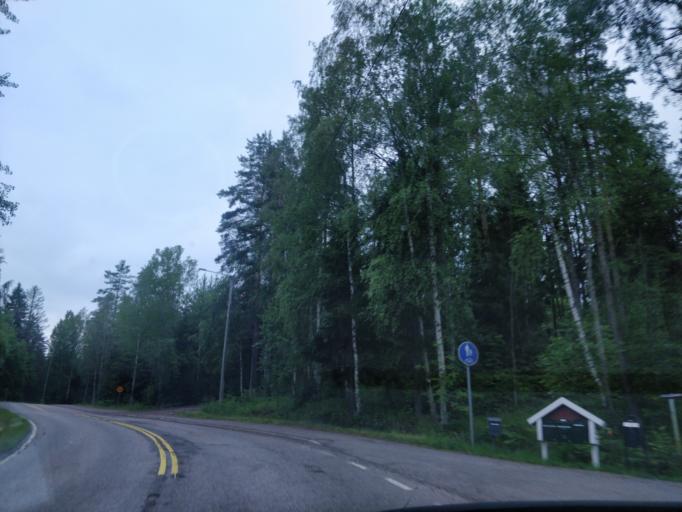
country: FI
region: Uusimaa
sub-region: Helsinki
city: Kauniainen
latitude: 60.3121
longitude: 24.7103
